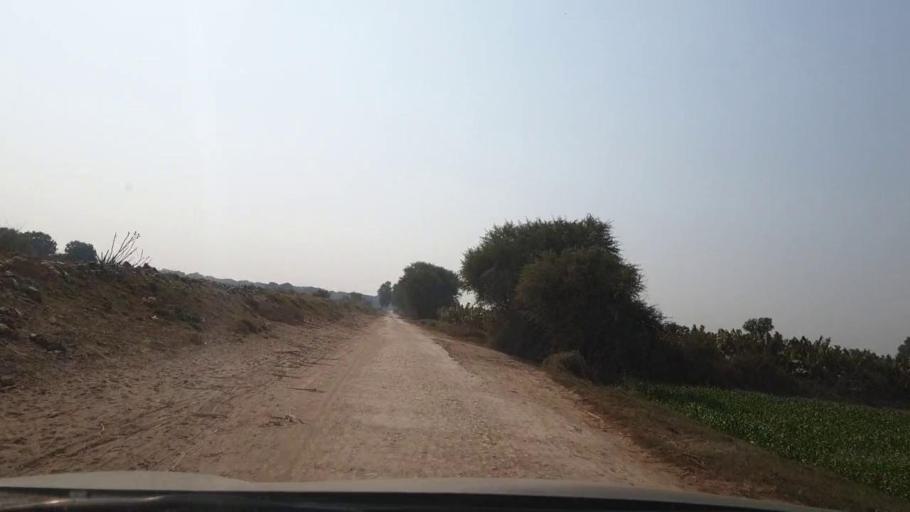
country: PK
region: Sindh
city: Tando Allahyar
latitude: 25.5031
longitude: 68.7860
